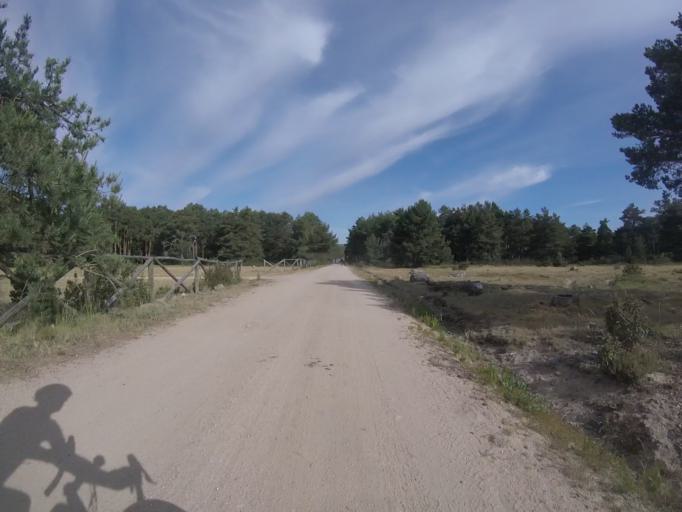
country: ES
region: Castille and Leon
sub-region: Provincia de Avila
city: Peguerinos
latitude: 40.6513
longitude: -4.1792
